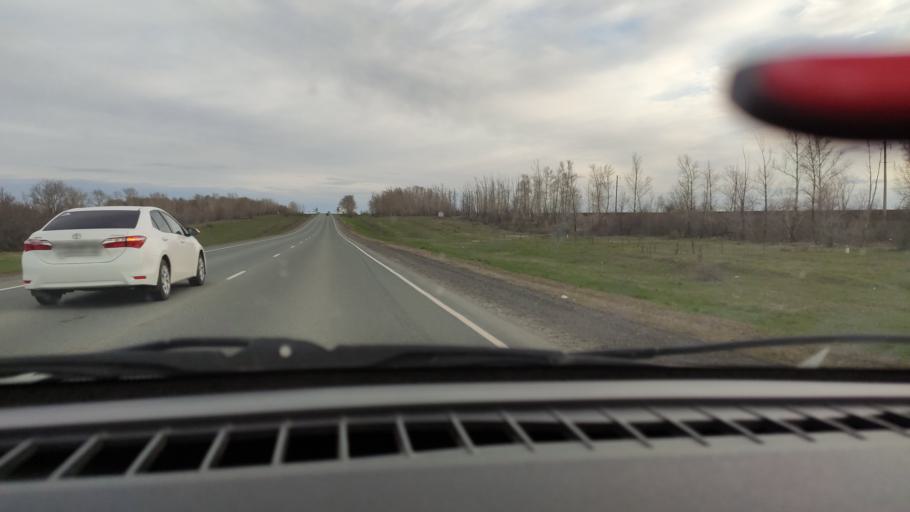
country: RU
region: Orenburg
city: Sakmara
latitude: 52.1504
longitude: 55.2860
